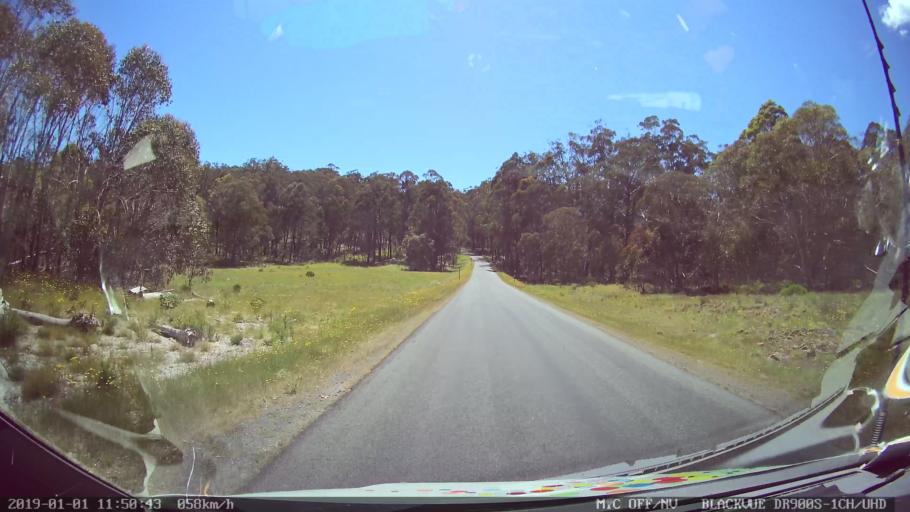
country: AU
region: New South Wales
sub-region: Snowy River
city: Jindabyne
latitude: -35.8897
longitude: 148.4235
